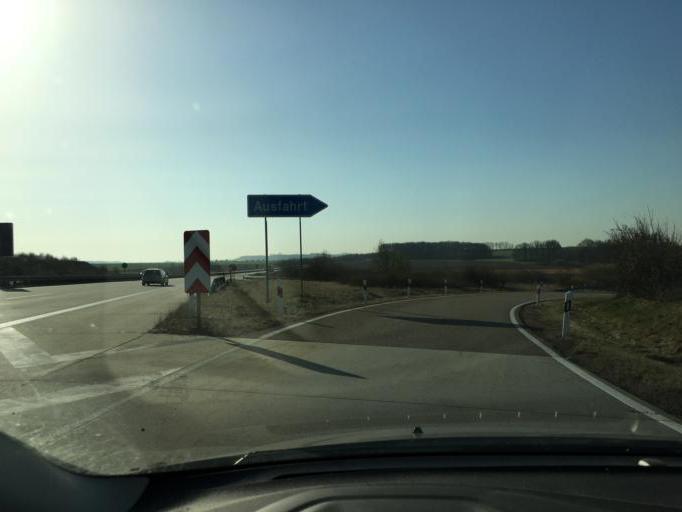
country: DE
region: Saxony
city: Niederfrohna
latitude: 50.9048
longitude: 12.7340
